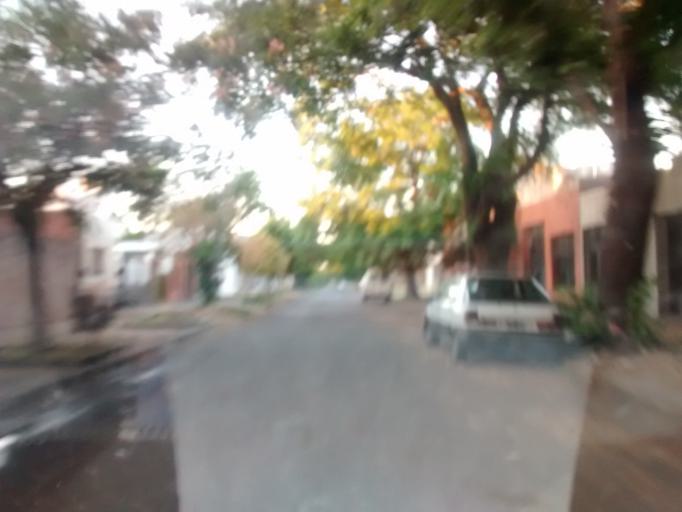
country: AR
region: Buenos Aires
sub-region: Partido de La Plata
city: La Plata
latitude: -34.9421
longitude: -57.9482
